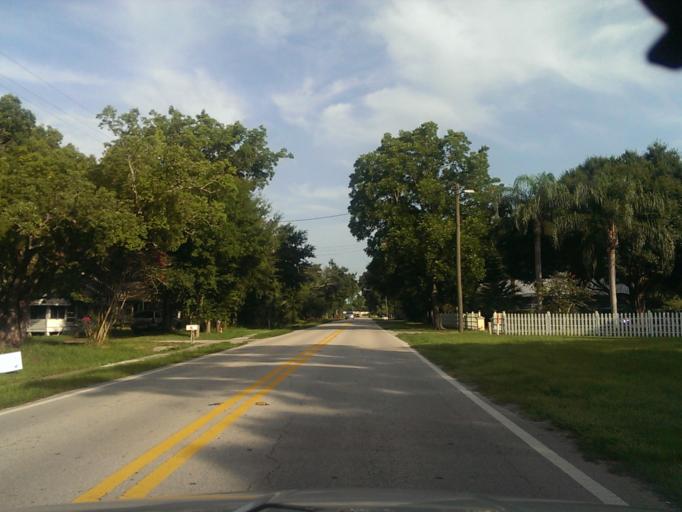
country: US
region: Florida
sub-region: Orange County
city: Winter Garden
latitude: 28.5500
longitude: -81.5724
